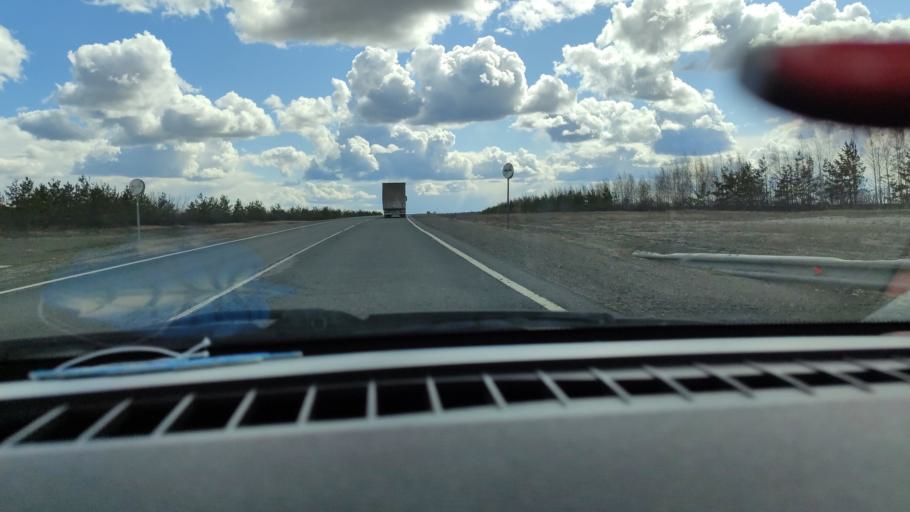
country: RU
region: Samara
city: Syzran'
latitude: 52.8803
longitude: 48.2917
